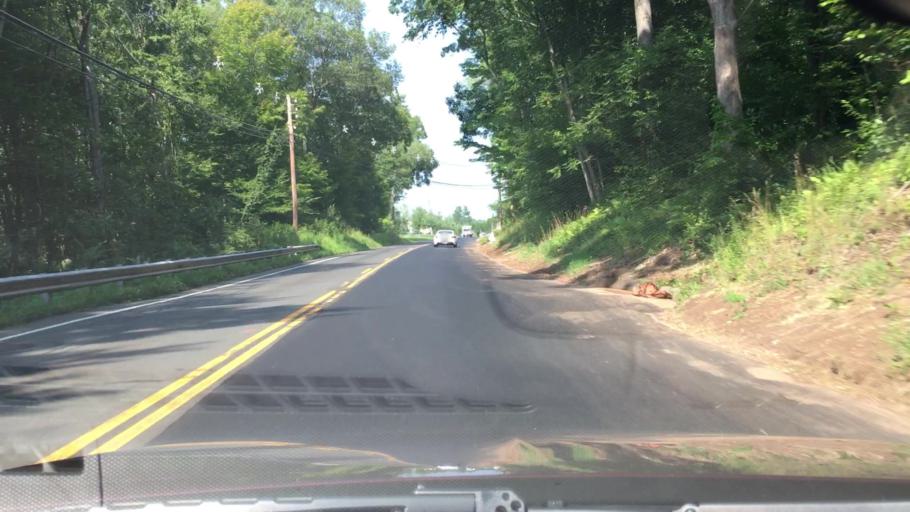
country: US
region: Connecticut
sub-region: Tolland County
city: Rockville
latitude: 41.8518
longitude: -72.4467
